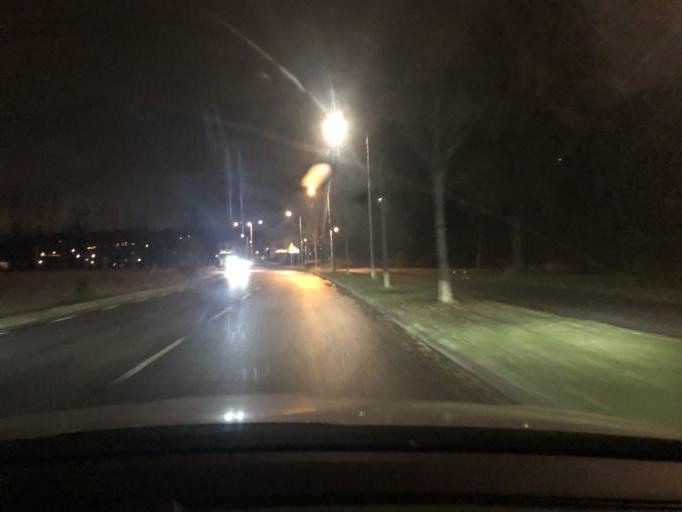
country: SE
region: Stockholm
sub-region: Huddinge Kommun
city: Huddinge
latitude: 59.2337
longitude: 17.9479
